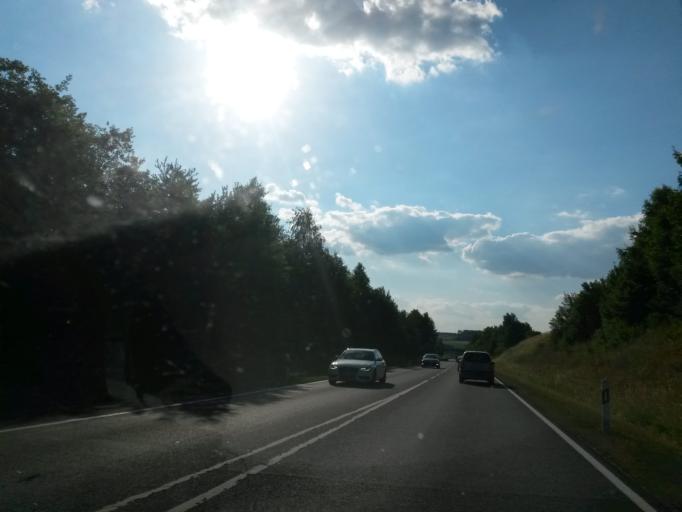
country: DE
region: Bavaria
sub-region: Regierungsbezirk Mittelfranken
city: Diespeck
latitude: 49.5853
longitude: 10.6332
